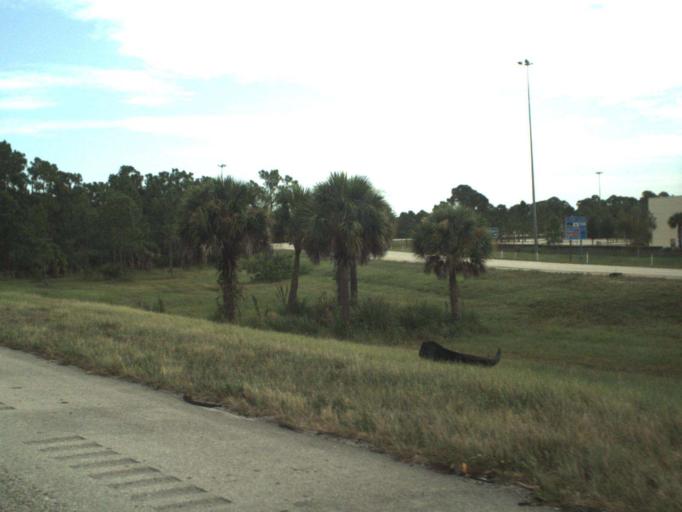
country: US
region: Florida
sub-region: Saint Lucie County
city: Port Saint Lucie
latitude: 27.2609
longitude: -80.4206
